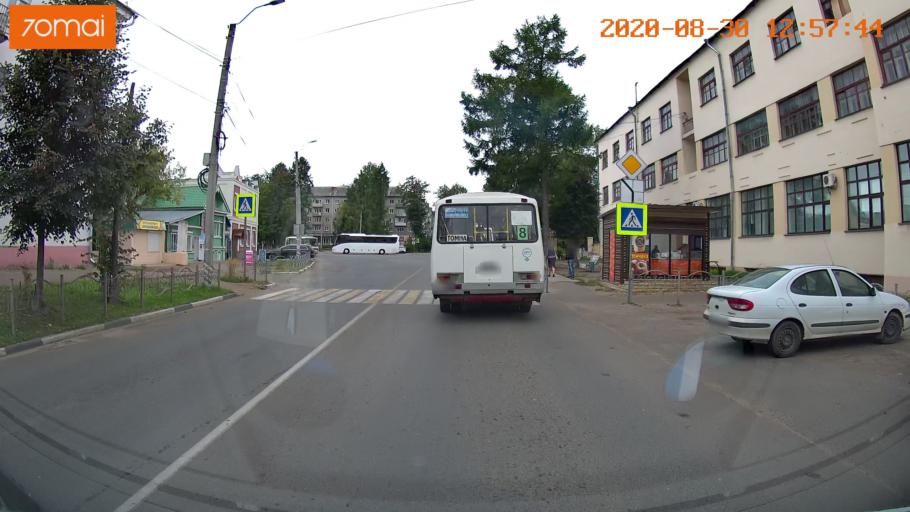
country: RU
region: Ivanovo
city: Kineshma
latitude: 57.4452
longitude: 42.1562
